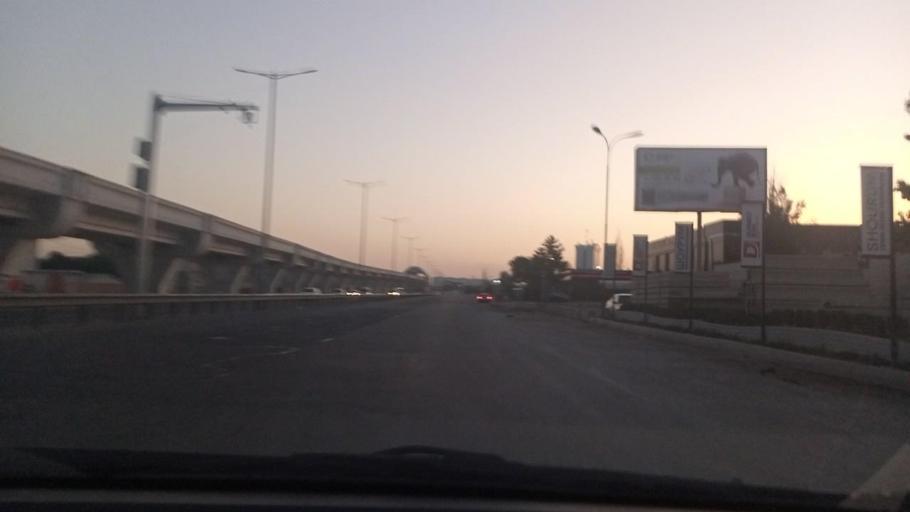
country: UZ
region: Toshkent Shahri
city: Bektemir
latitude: 41.2606
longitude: 69.3620
